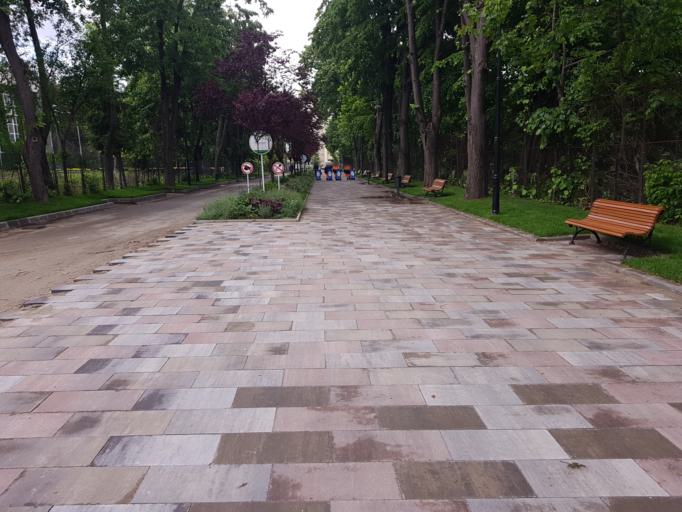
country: RO
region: Ilfov
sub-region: Comuna Fundeni-Dobroesti
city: Fundeni
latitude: 44.4347
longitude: 26.1482
